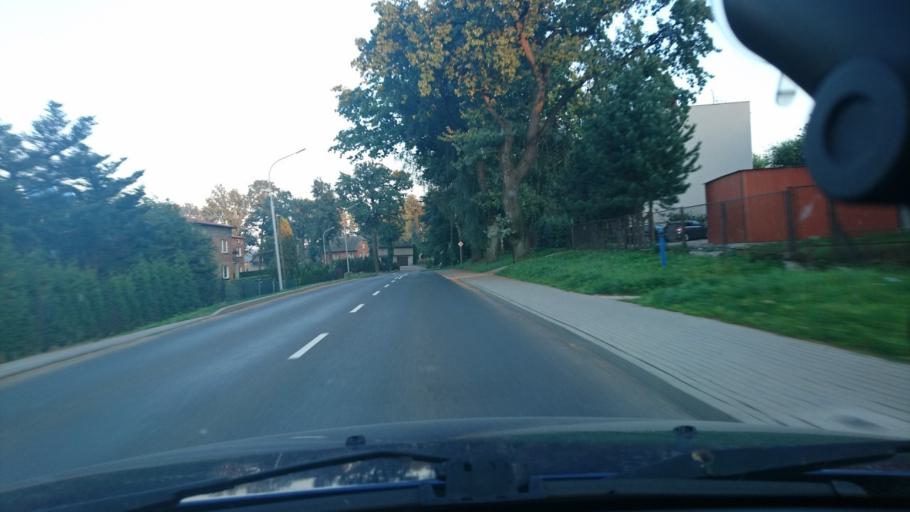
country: PL
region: Silesian Voivodeship
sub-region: Powiat bielski
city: Bestwina
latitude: 49.8967
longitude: 19.0635
